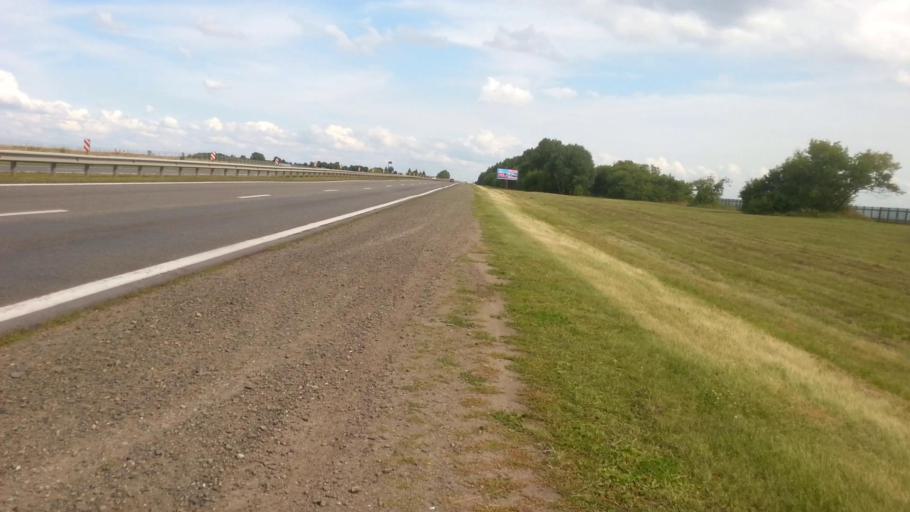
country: RU
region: Altai Krai
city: Nauchnyy Gorodok
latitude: 53.3561
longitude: 83.5140
